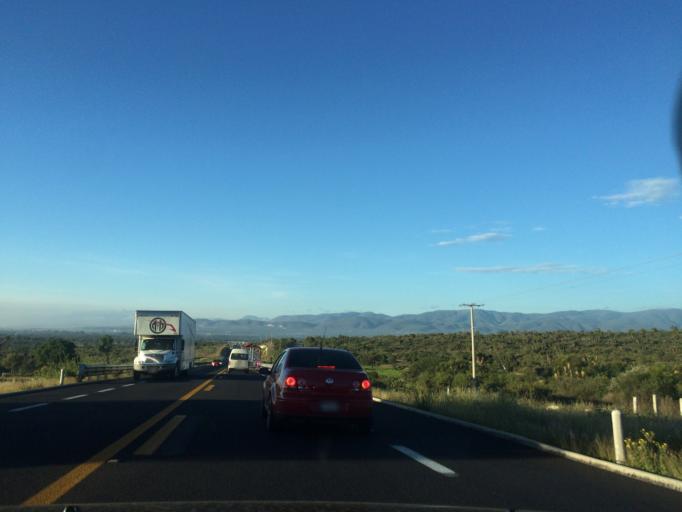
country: MX
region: Puebla
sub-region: Tehuacan
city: Magdalena Cuayucatepec
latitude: 18.5676
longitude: -97.4639
